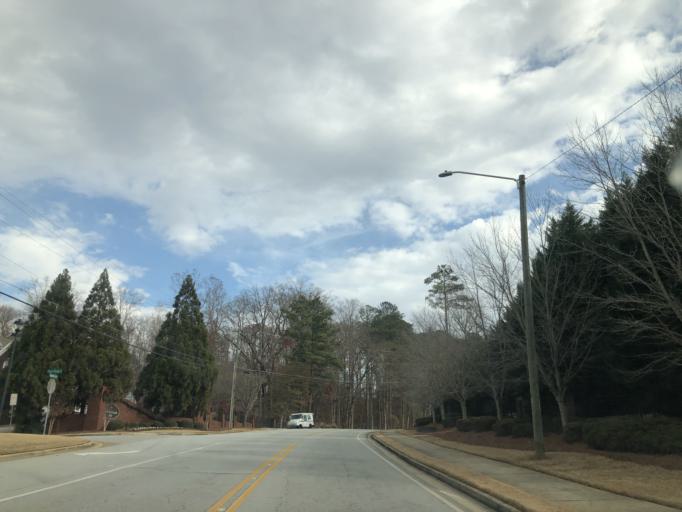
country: US
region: Georgia
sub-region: DeKalb County
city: Panthersville
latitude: 33.6654
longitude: -84.2069
